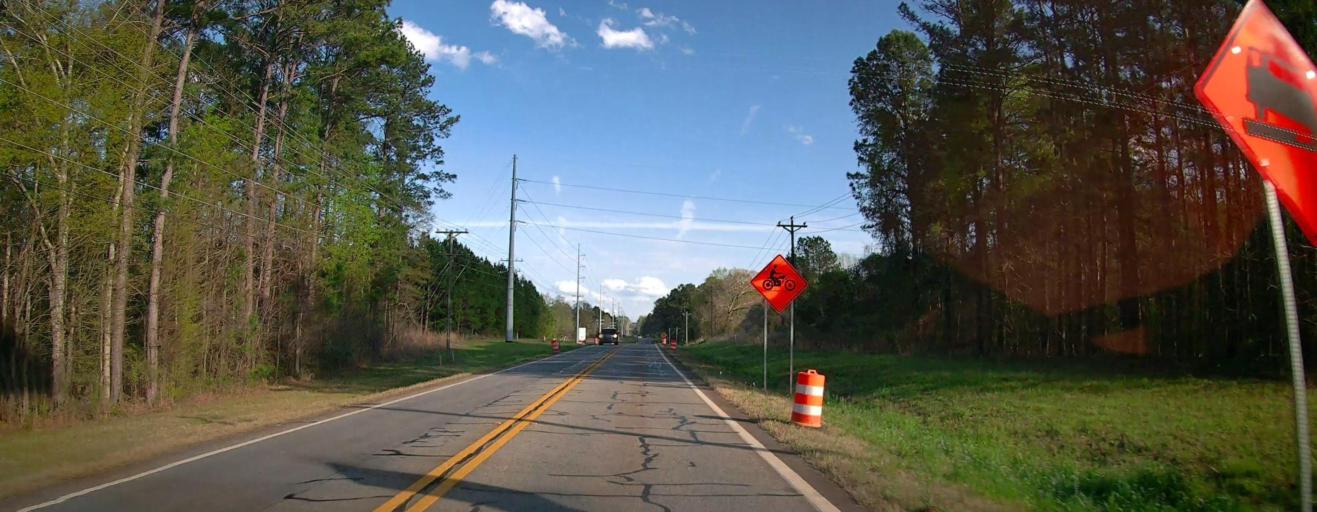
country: US
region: Georgia
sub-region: Baldwin County
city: Milledgeville
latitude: 33.1562
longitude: -83.3501
